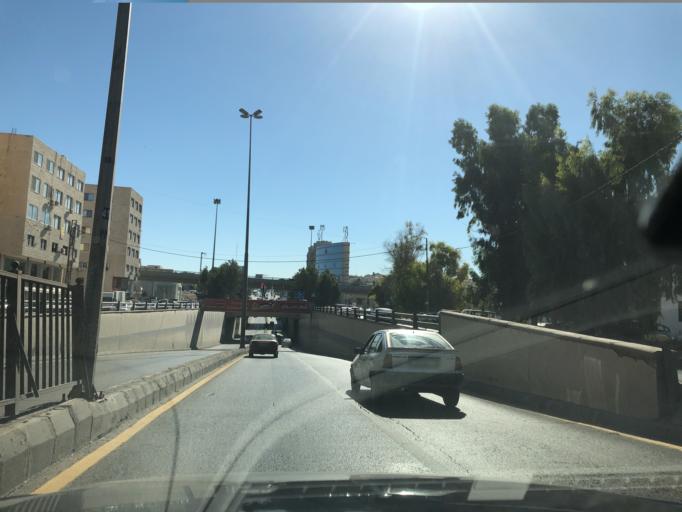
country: JO
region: Amman
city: Wadi as Sir
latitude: 31.9750
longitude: 35.8634
